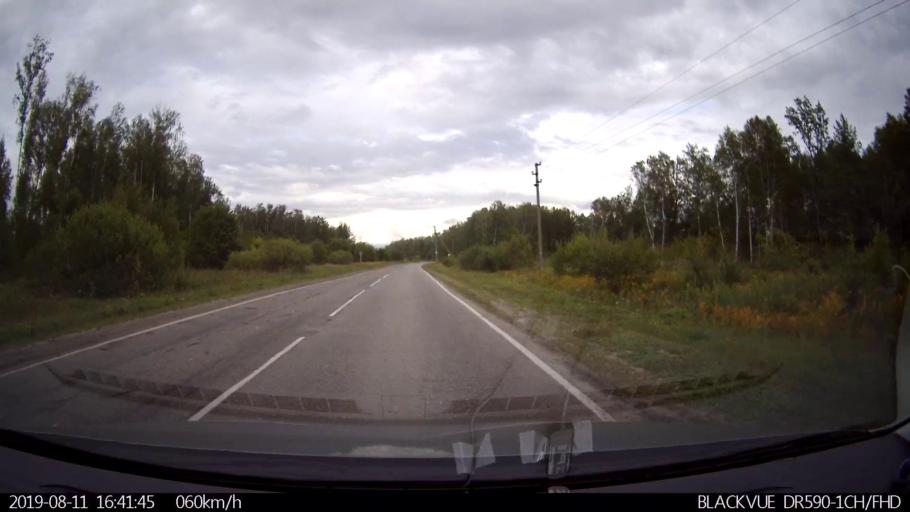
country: RU
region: Ulyanovsk
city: Mayna
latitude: 54.1555
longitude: 47.6558
